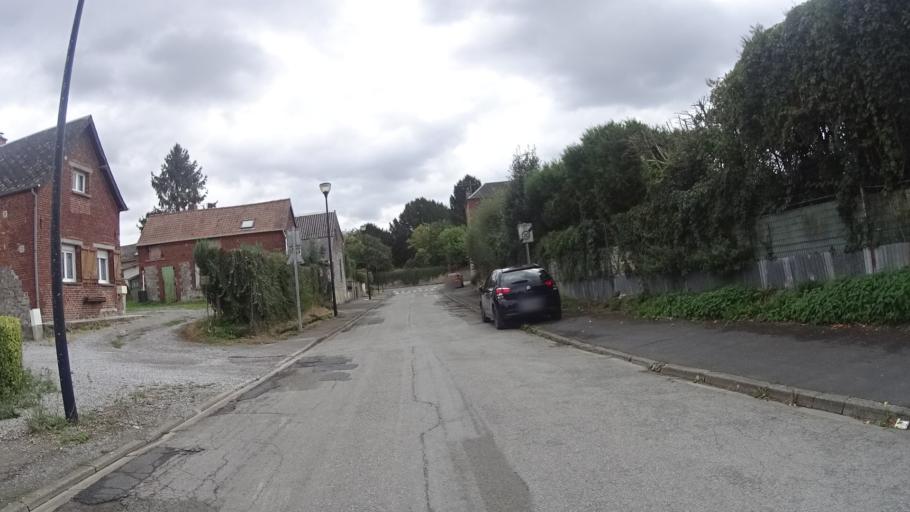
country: FR
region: Nord-Pas-de-Calais
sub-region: Departement du Nord
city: Aulnoye-Aymeries
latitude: 50.2127
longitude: 3.8311
